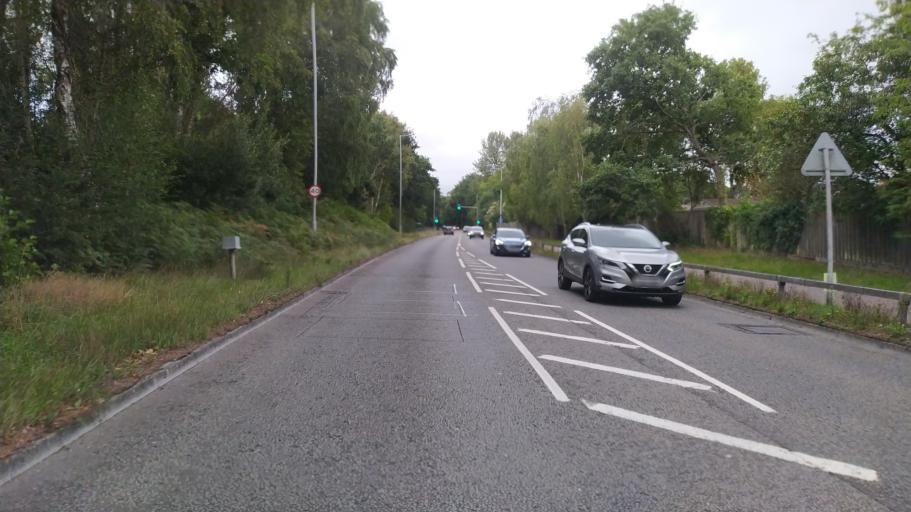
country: GB
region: England
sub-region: Dorset
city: Broadstone
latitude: 50.7524
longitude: -2.0024
